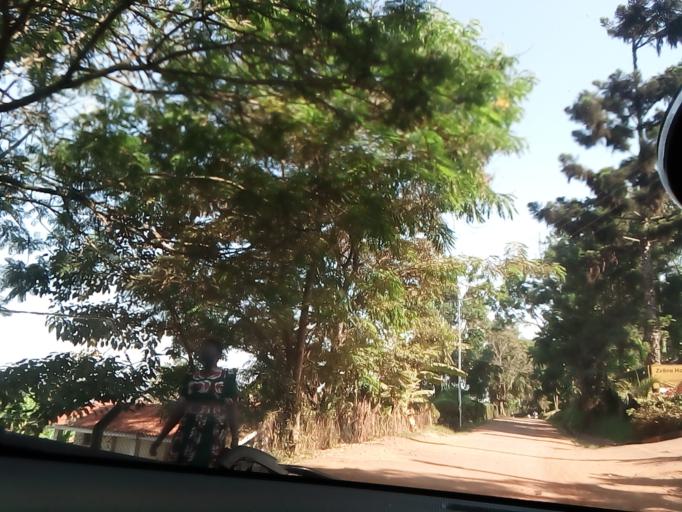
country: UG
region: Central Region
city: Masaka
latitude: -0.3394
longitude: 31.7355
